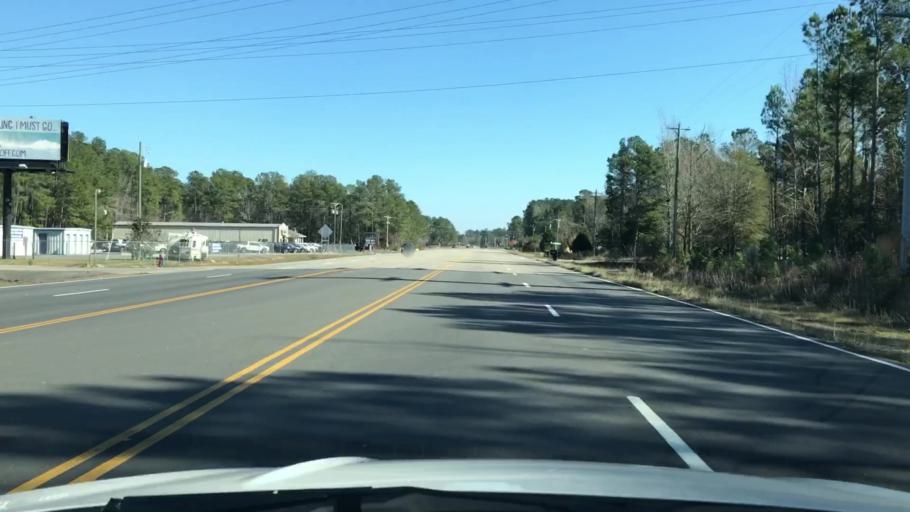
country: US
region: South Carolina
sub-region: Horry County
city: Garden City
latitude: 33.6296
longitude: -79.0329
